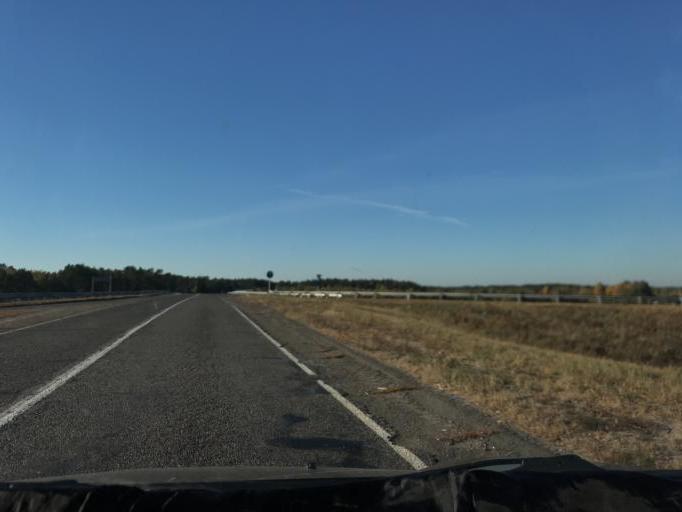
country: BY
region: Gomel
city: Kalinkavichy
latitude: 52.0723
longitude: 29.3633
